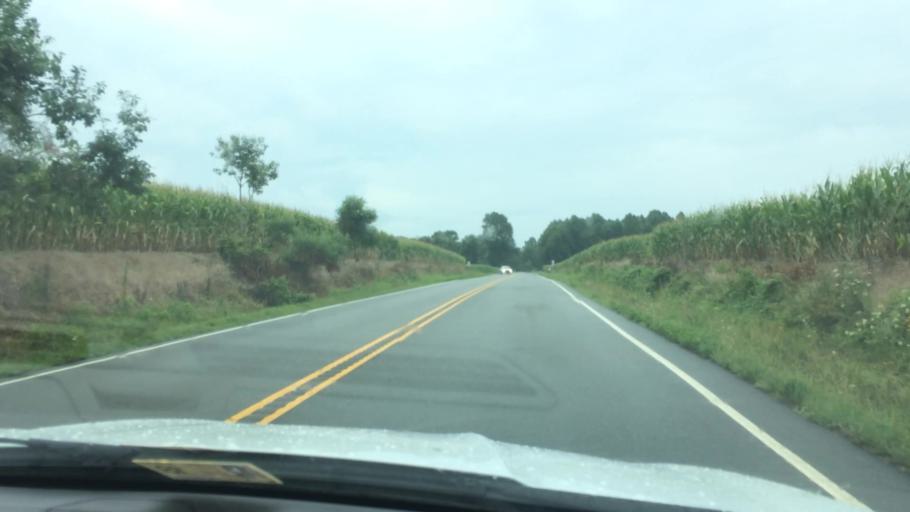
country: US
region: Virginia
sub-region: King William County
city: West Point
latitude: 37.5723
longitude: -76.7562
